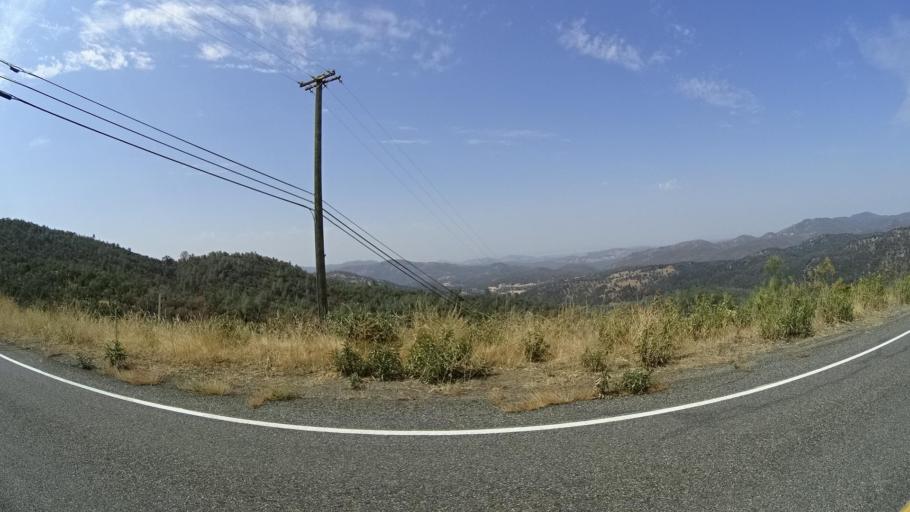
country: US
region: California
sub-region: Tuolumne County
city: Tuolumne City
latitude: 37.7348
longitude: -120.1664
